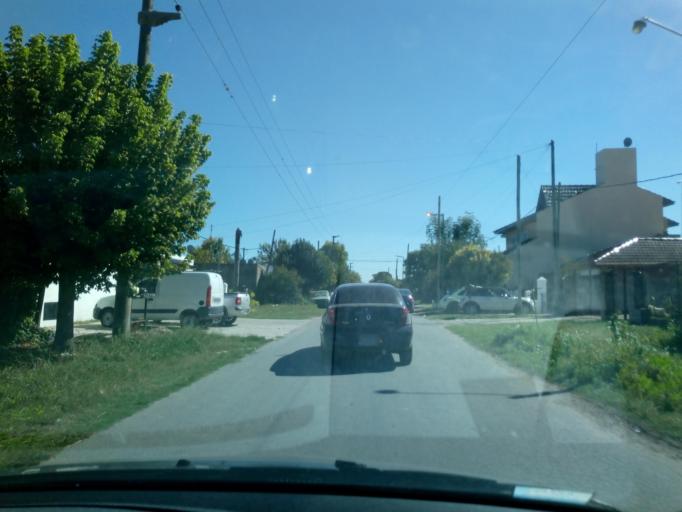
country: AR
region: Buenos Aires
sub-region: Partido de La Plata
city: La Plata
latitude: -35.0004
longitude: -58.0484
